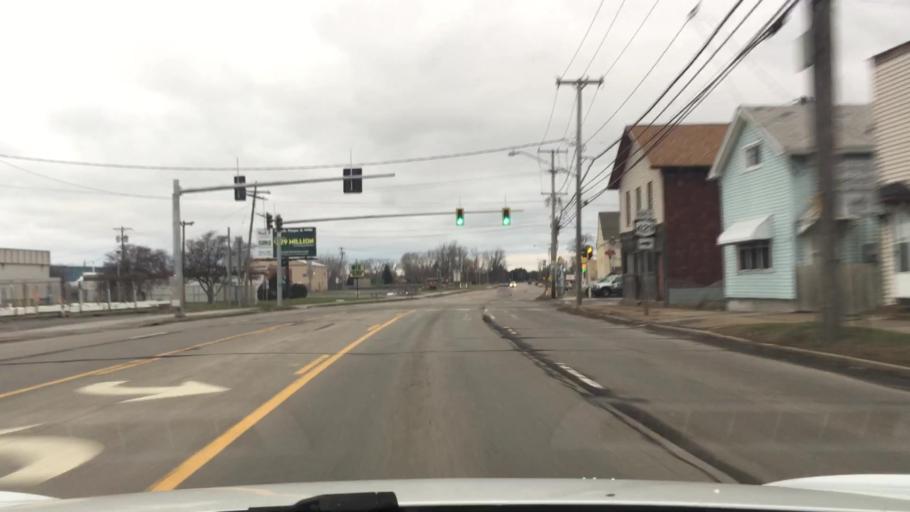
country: US
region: New York
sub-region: Erie County
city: Tonawanda
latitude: 43.0342
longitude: -78.8837
